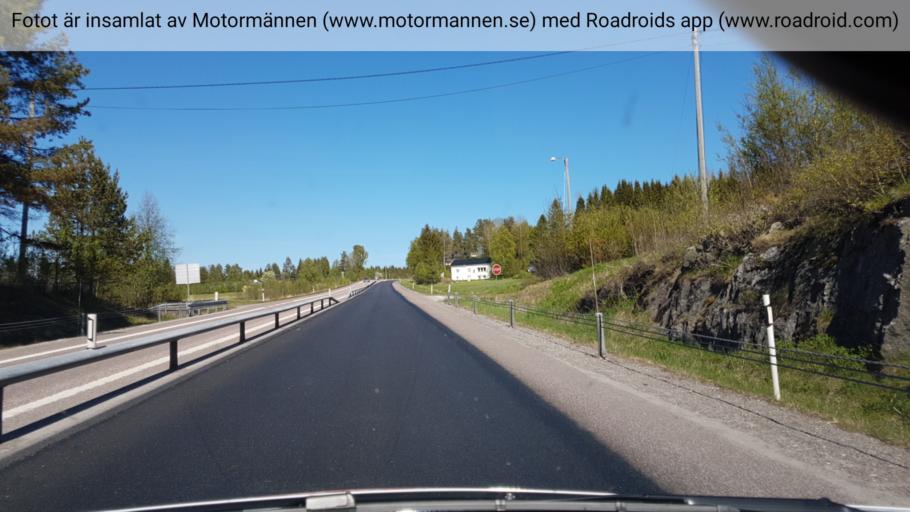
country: SE
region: Vaesternorrland
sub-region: OErnskoeldsviks Kommun
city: Husum
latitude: 63.3323
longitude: 19.0613
